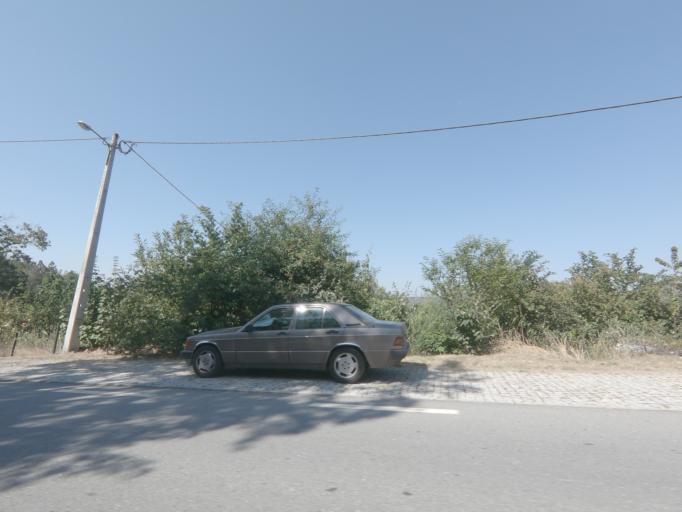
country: PT
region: Viseu
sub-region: Tarouca
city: Tarouca
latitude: 41.0366
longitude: -7.7324
